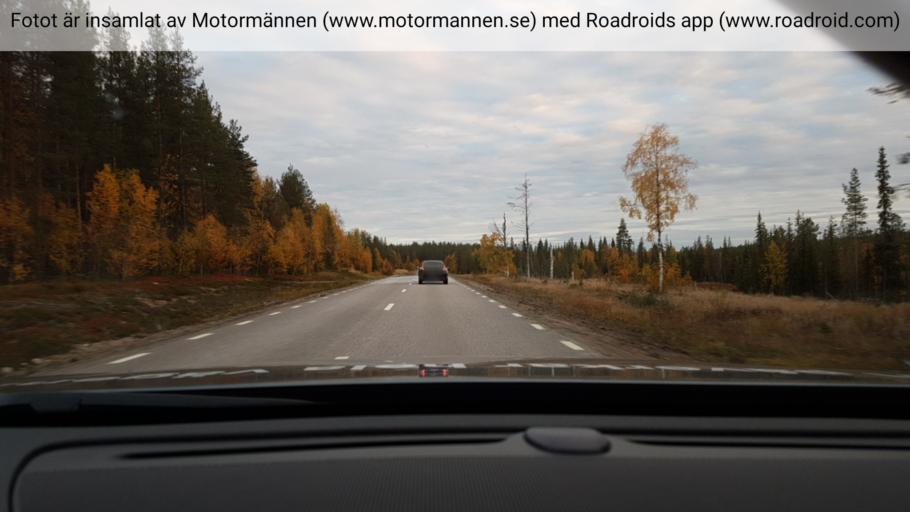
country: SE
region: Norrbotten
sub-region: Jokkmokks Kommun
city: Jokkmokk
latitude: 66.0826
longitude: 20.0732
